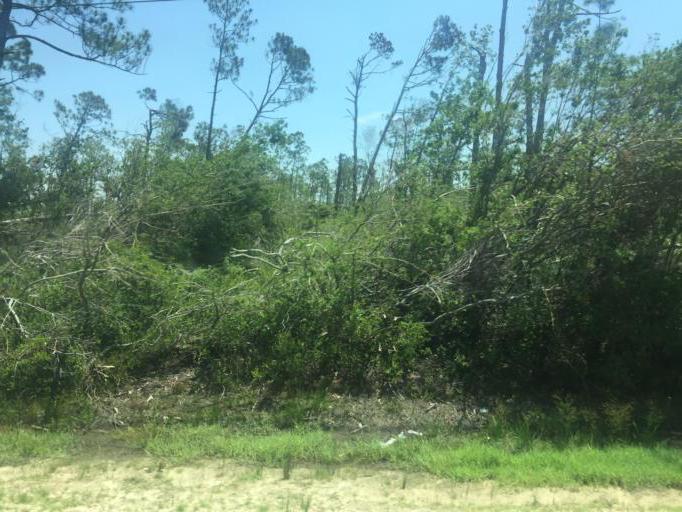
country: US
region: Florida
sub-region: Bay County
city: Lynn Haven
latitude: 30.2151
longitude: -85.6663
